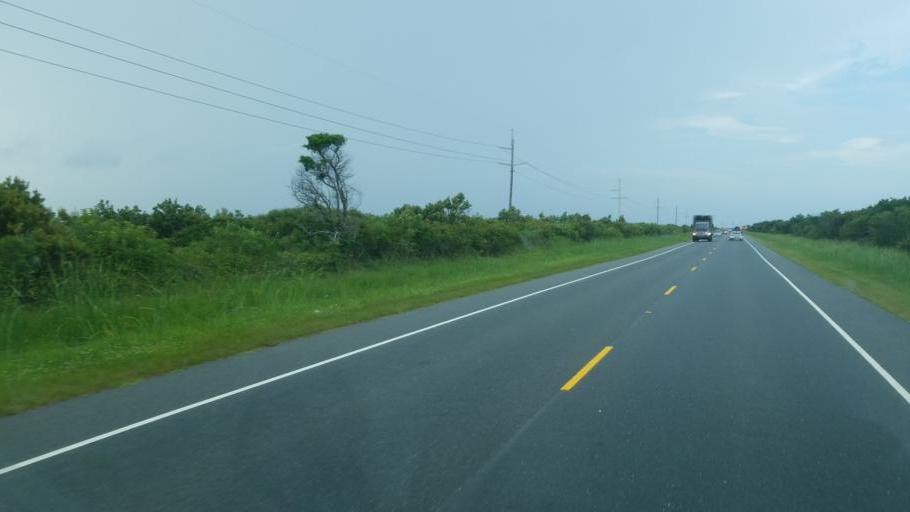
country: US
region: North Carolina
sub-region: Dare County
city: Wanchese
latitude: 35.6509
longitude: -75.4766
